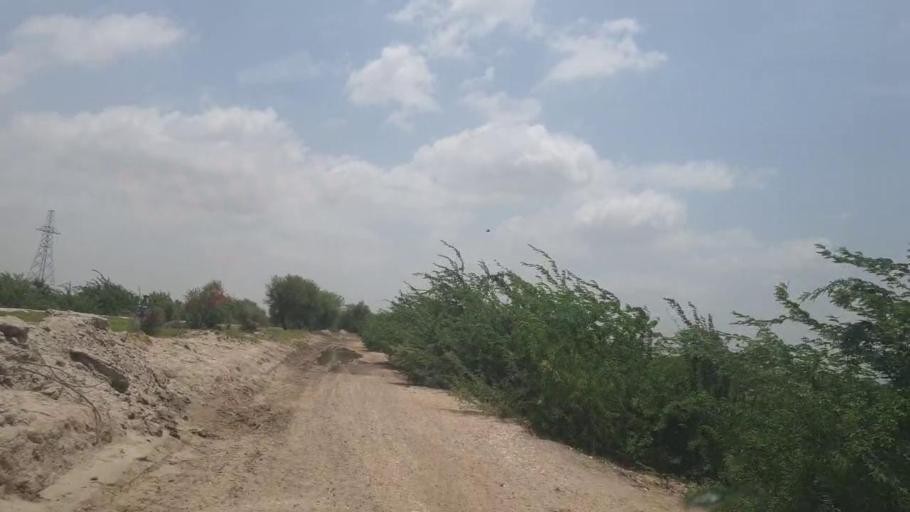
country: PK
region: Sindh
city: Tando Mittha Khan
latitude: 25.9161
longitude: 69.2328
